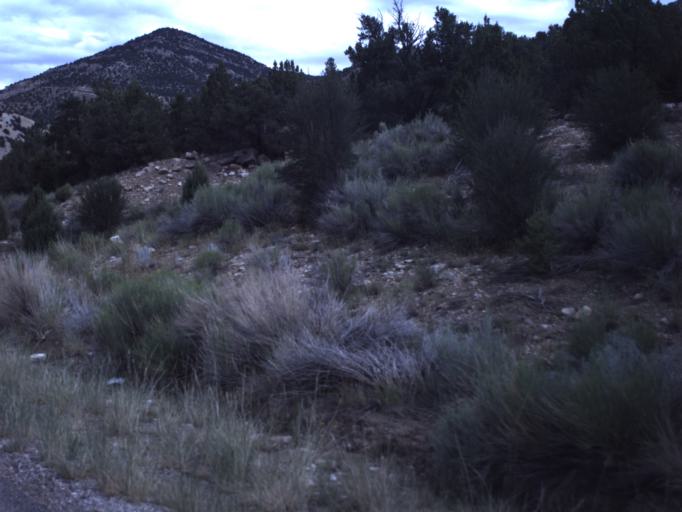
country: US
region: Utah
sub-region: Iron County
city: Cedar City
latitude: 37.6585
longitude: -112.9936
